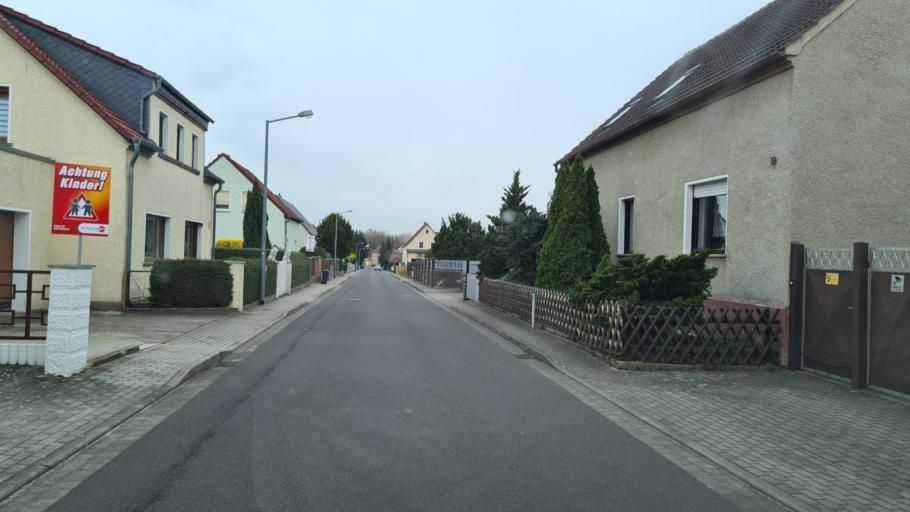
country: DE
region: Brandenburg
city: Lauchhammer
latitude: 51.4961
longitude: 13.7846
